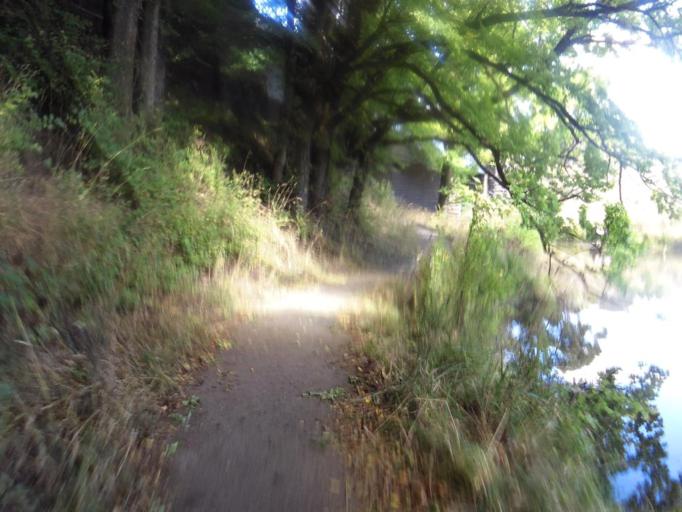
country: AU
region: Victoria
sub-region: Mount Alexander
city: Castlemaine
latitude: -37.2553
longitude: 144.4518
